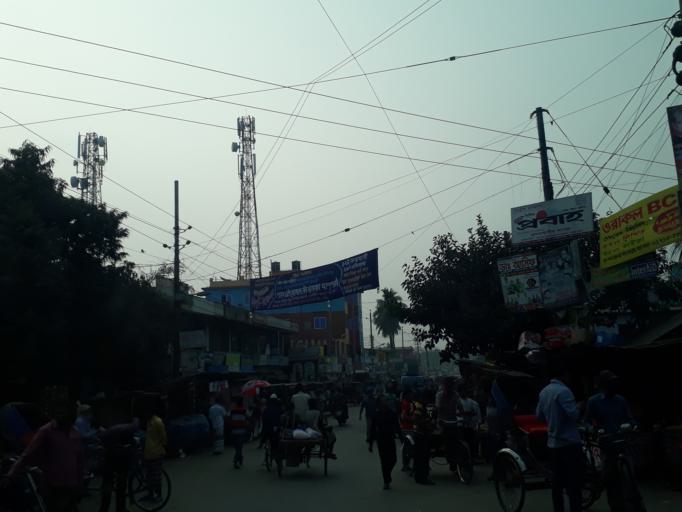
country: BD
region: Khulna
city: Khulna
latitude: 22.8968
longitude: 89.5098
